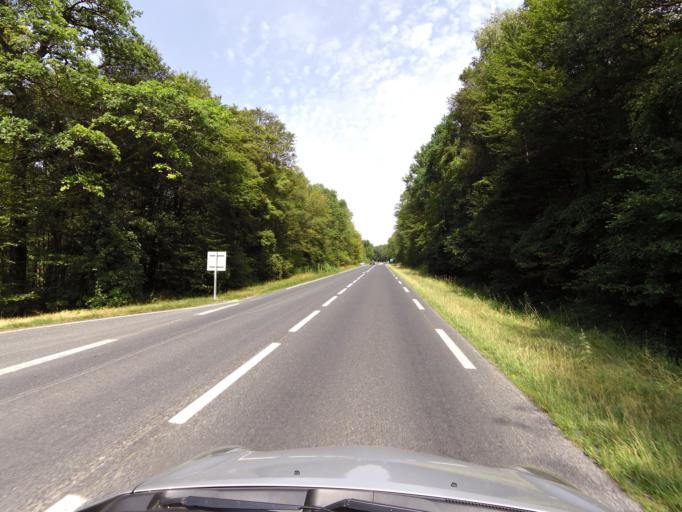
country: FR
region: Champagne-Ardenne
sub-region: Departement de la Marne
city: Rilly-la-Montagne
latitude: 49.1507
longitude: 4.0095
